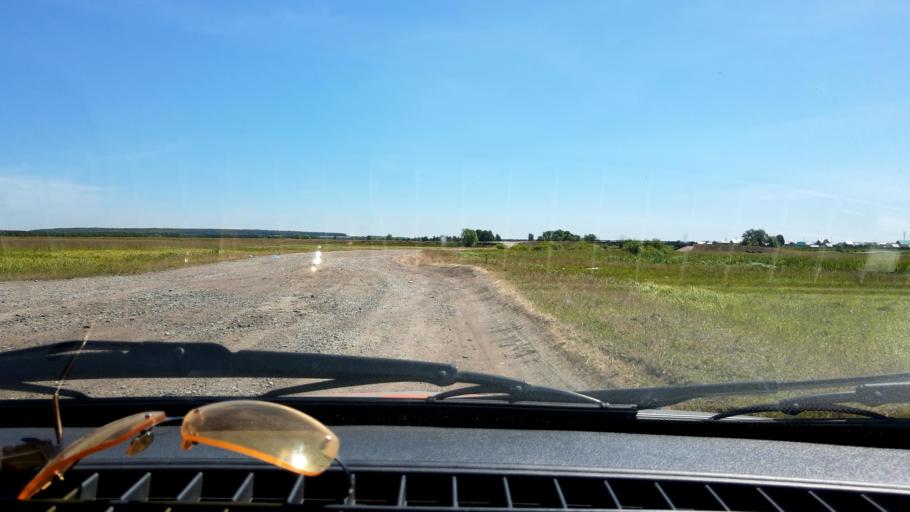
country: RU
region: Bashkortostan
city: Mikhaylovka
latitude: 54.9680
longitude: 55.7983
